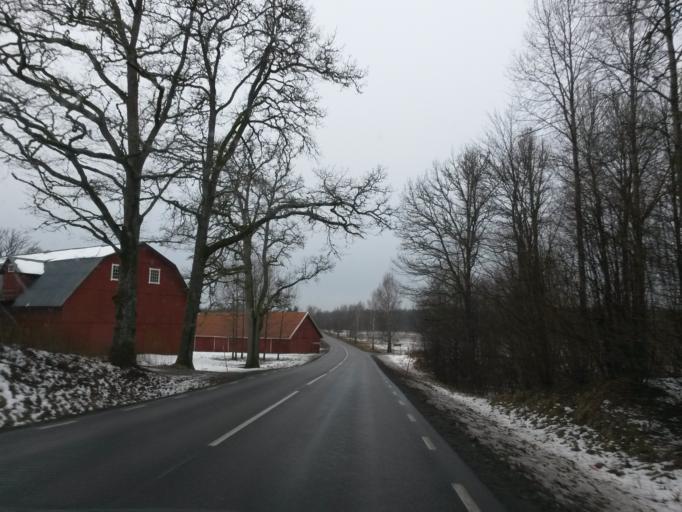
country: SE
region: Vaestra Goetaland
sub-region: Tranemo Kommun
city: Langhem
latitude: 57.6794
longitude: 13.3242
